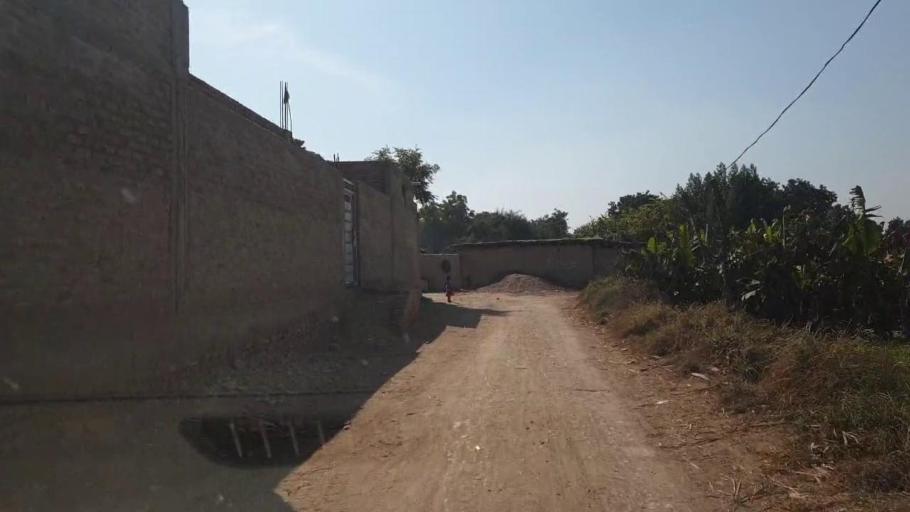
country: PK
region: Sindh
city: Tando Allahyar
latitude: 25.3887
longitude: 68.7807
